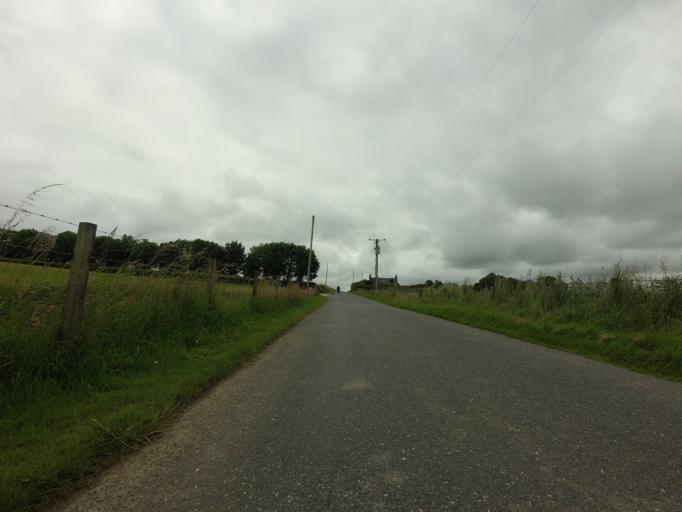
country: GB
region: Scotland
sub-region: Aberdeenshire
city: Turriff
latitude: 57.5352
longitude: -2.4316
